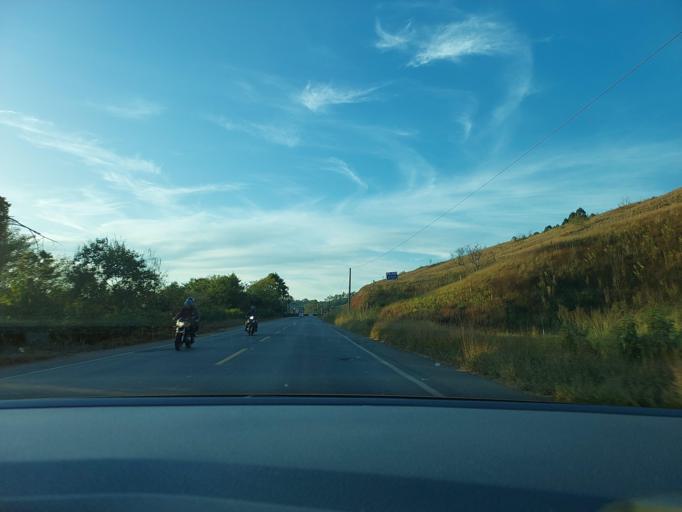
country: BR
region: Minas Gerais
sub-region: Vicosa
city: Vicosa
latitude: -20.7935
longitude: -42.8380
